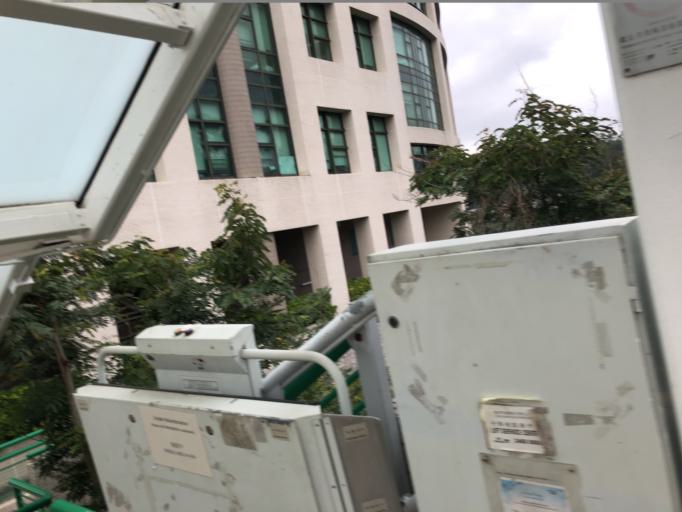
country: HK
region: Tai Po
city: Tai Po
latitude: 22.4667
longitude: 114.1937
